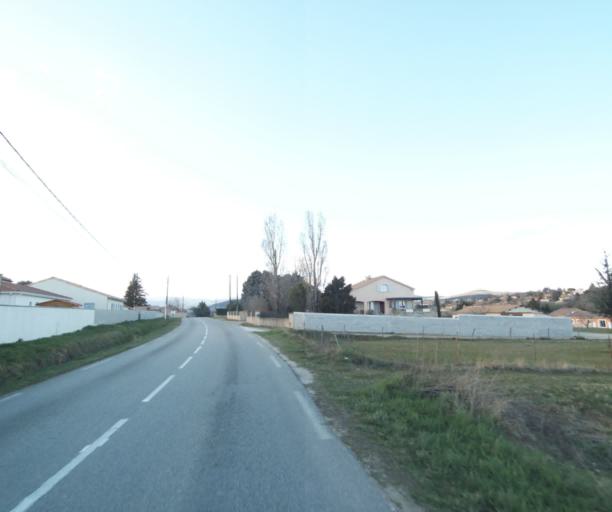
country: FR
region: Rhone-Alpes
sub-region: Departement de l'Ardeche
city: Davezieux
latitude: 45.2458
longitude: 4.7087
